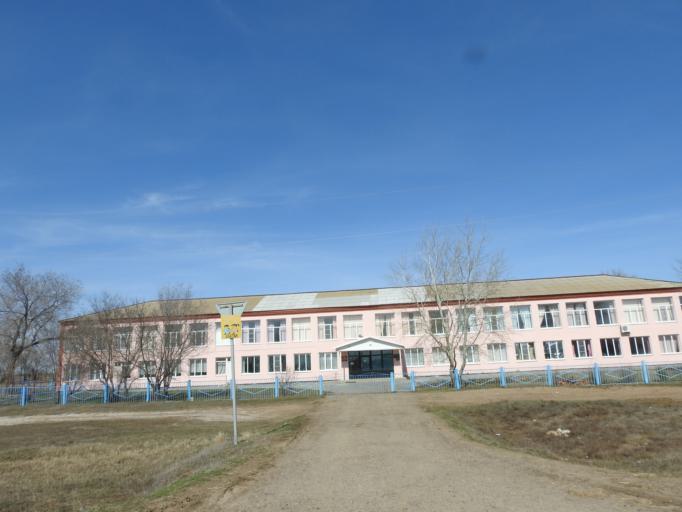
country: RU
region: Volgograd
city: Staraya Poltavka
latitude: 50.4284
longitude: 46.3885
